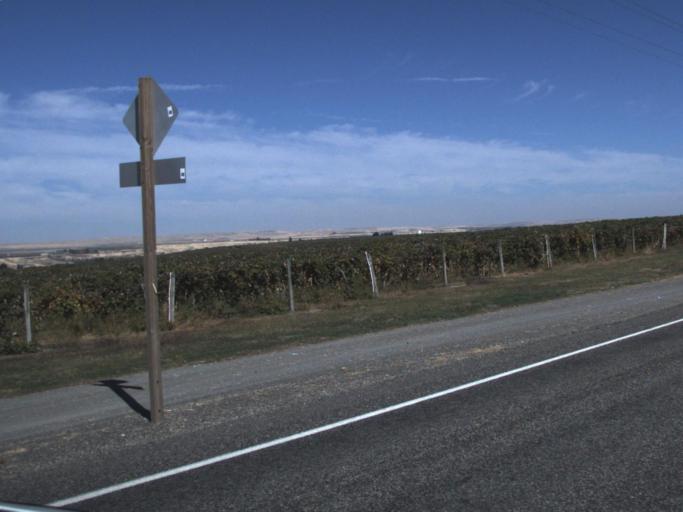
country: US
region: Washington
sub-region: Walla Walla County
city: Burbank
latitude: 46.2322
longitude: -118.8445
